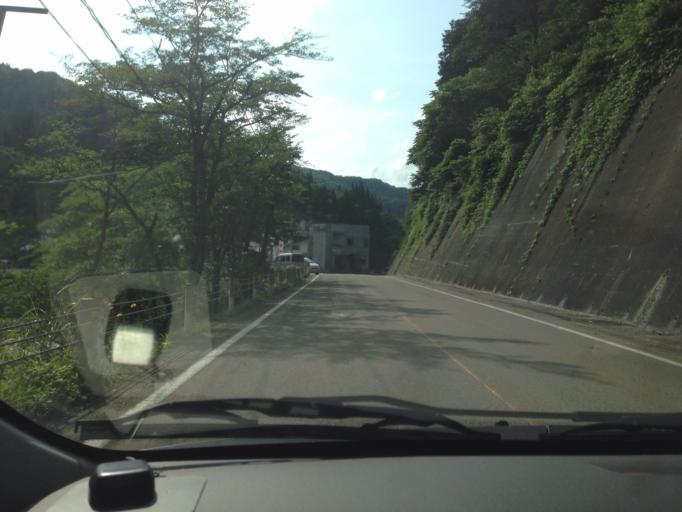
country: JP
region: Fukushima
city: Kitakata
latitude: 37.4213
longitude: 139.5462
